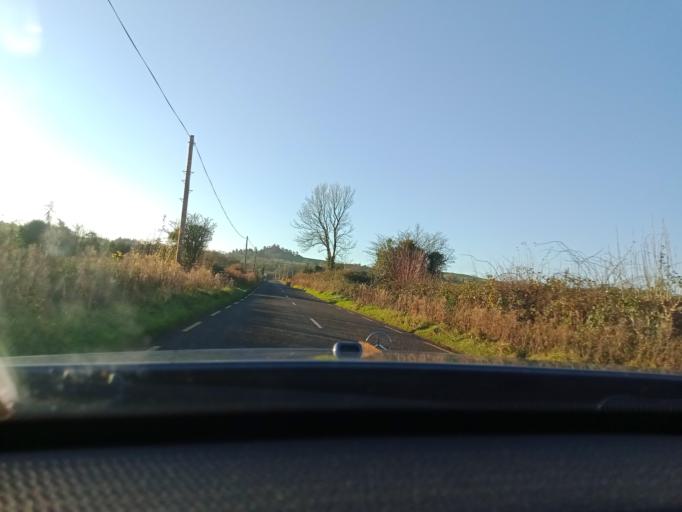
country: IE
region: Leinster
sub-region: Kilkenny
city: Callan
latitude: 52.4713
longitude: -7.3943
